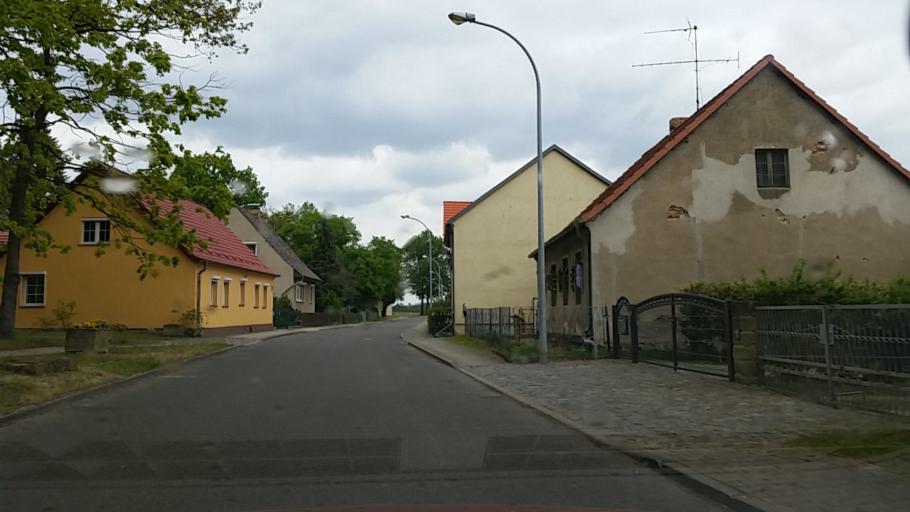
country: DE
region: Brandenburg
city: Rauen
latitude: 52.3136
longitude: 13.9645
